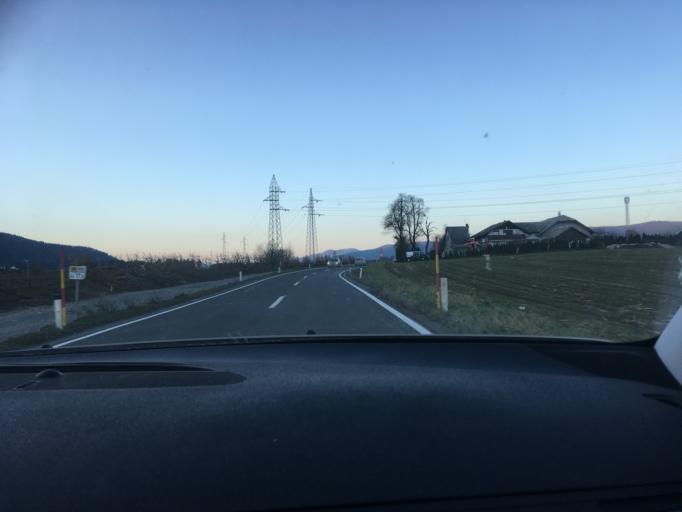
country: SI
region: Kocevje
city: Kocevje
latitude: 45.6657
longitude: 14.8389
